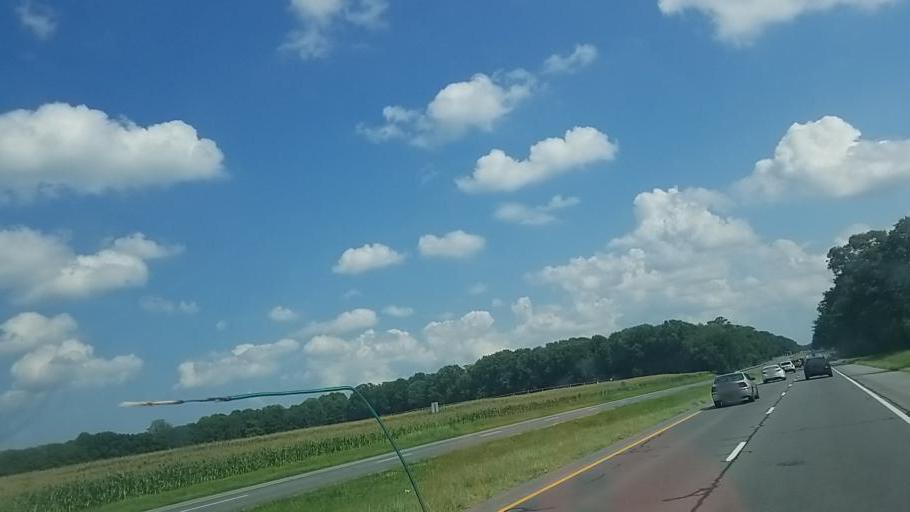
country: US
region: Delaware
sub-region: Sussex County
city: Millsboro
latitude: 38.6173
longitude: -75.3346
